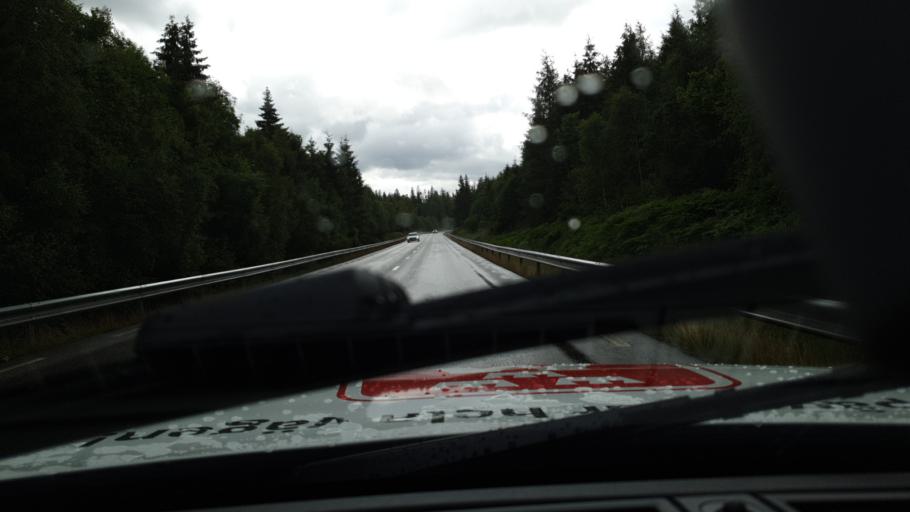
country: SE
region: Kronoberg
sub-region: Vaxjo Kommun
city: Lammhult
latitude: 57.1305
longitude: 14.6222
